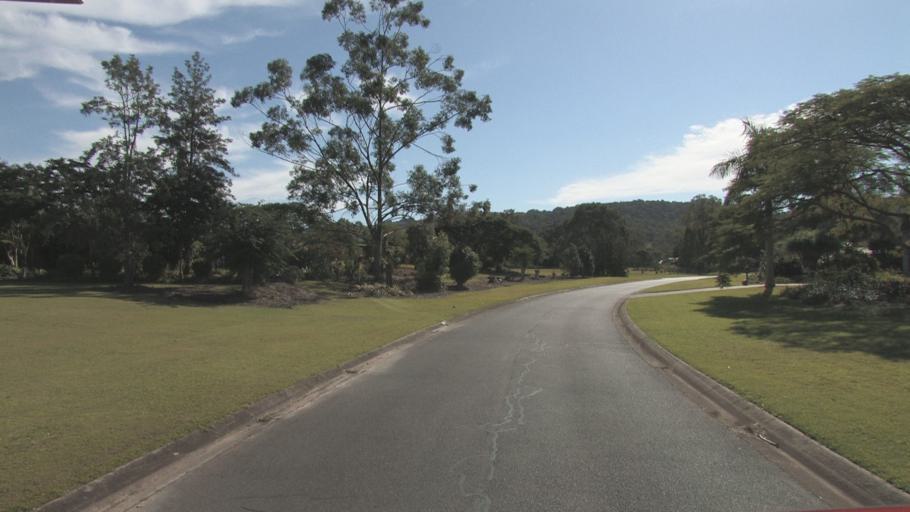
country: AU
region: Queensland
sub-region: Logan
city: Windaroo
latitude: -27.7598
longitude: 153.1820
